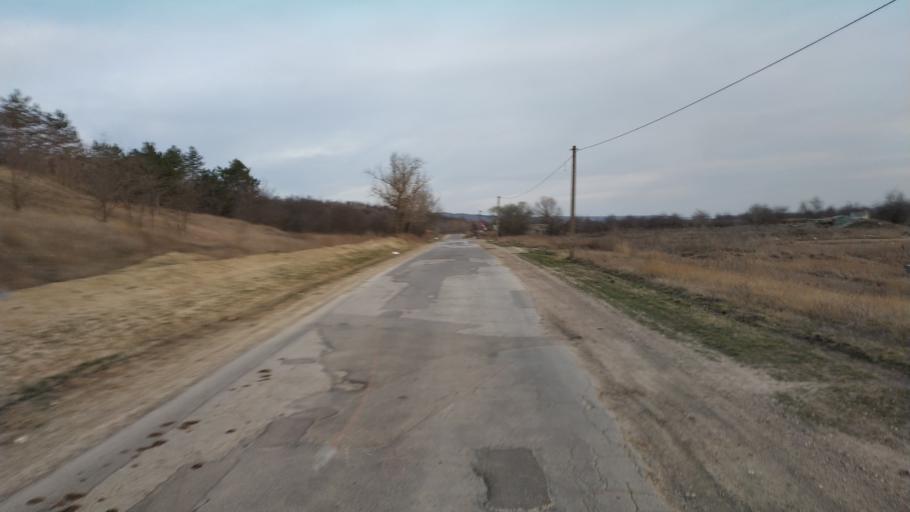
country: MD
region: Hincesti
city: Dancu
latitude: 46.7952
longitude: 28.1835
